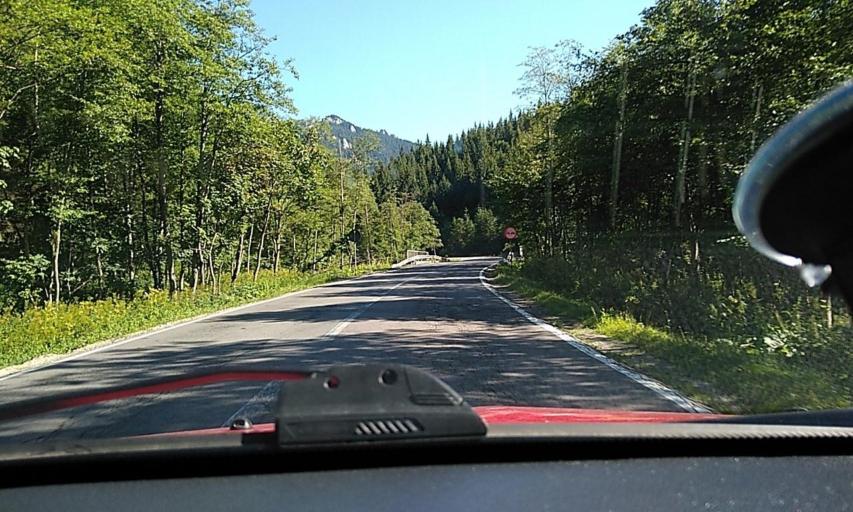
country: RO
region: Brasov
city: Crivina
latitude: 45.4793
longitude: 25.9202
